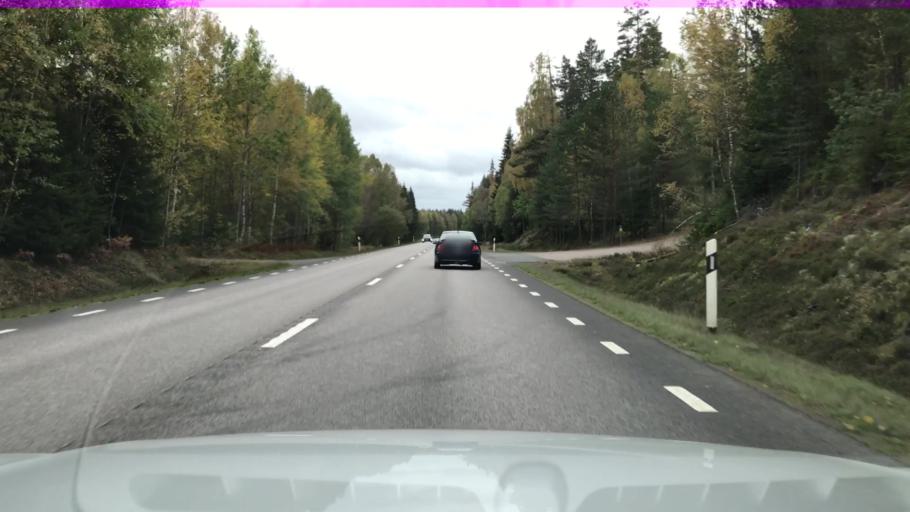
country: SE
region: Kalmar
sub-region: Hultsfreds Kommun
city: Hultsfred
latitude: 57.5460
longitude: 15.8458
